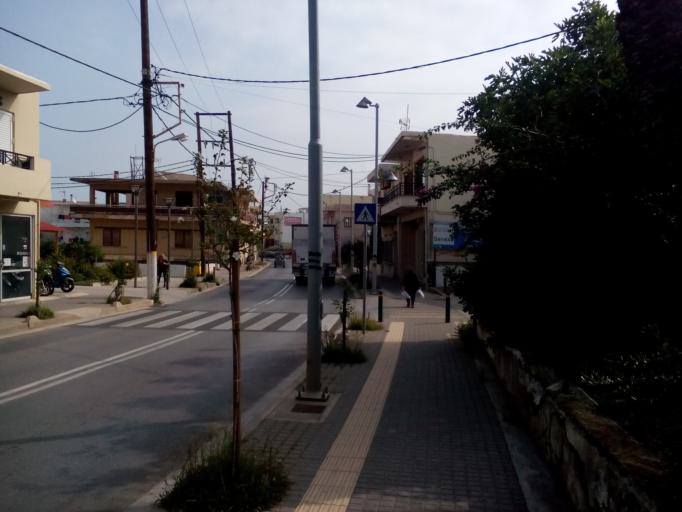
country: GR
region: Crete
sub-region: Nomos Rethymnis
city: Rethymno
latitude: 35.3656
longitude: 24.4975
